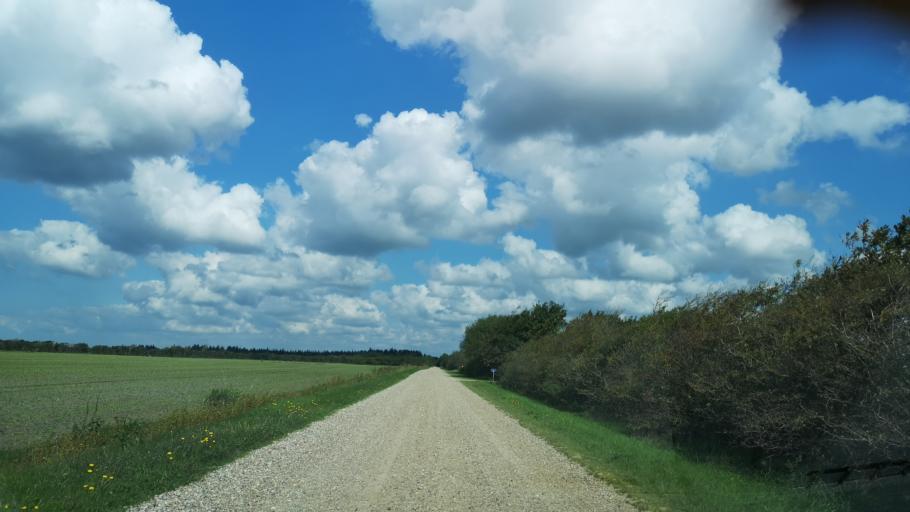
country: DK
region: Central Jutland
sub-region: Ringkobing-Skjern Kommune
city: Skjern
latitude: 55.8581
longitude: 8.3865
